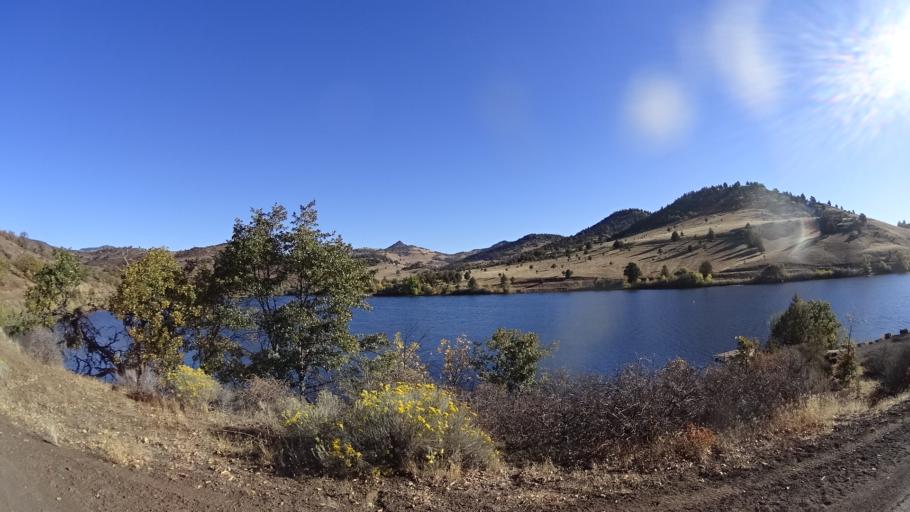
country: US
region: California
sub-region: Siskiyou County
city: Montague
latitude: 41.9689
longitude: -122.4388
